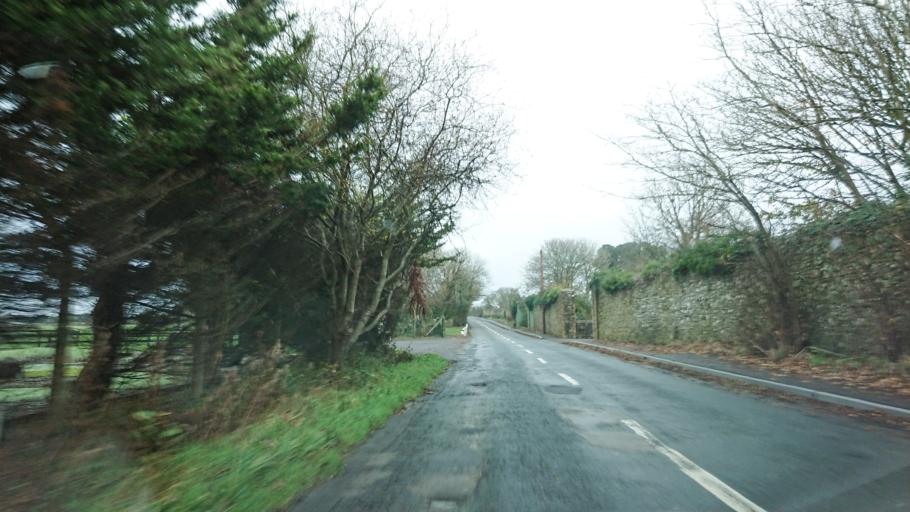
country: IE
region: Munster
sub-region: Waterford
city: Tra Mhor
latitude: 52.1485
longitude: -7.1718
